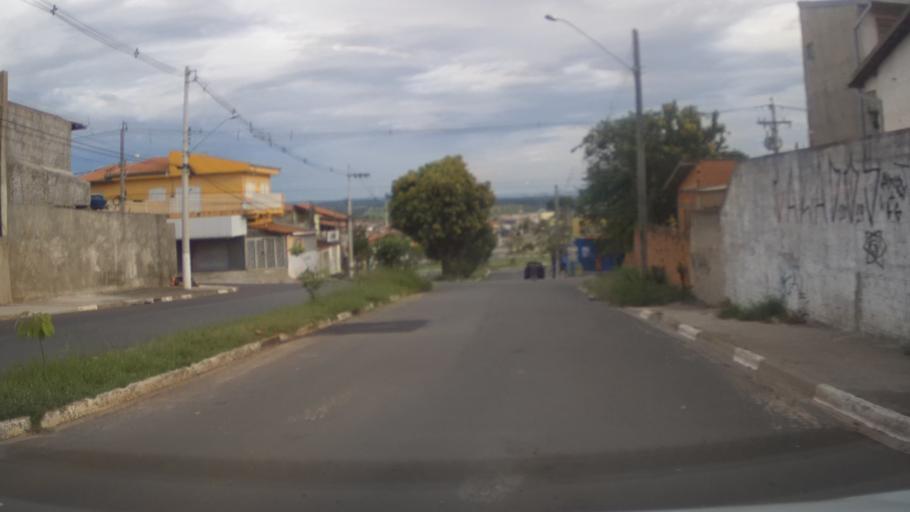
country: BR
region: Sao Paulo
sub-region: Hortolandia
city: Hortolandia
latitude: -22.9560
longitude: -47.2003
